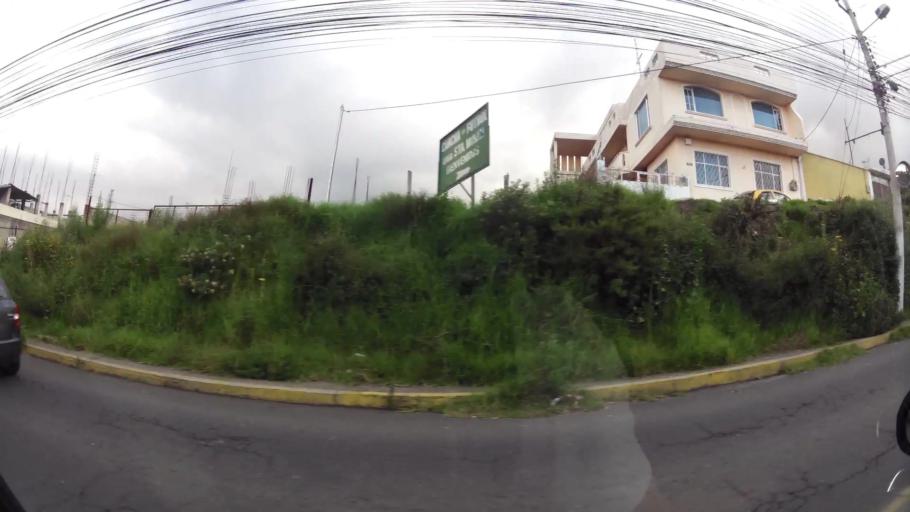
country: EC
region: Pichincha
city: Sangolqui
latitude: -0.2906
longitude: -78.4886
